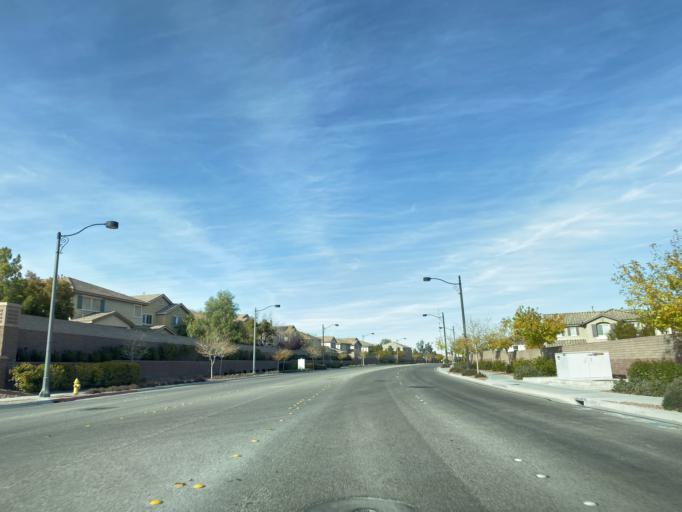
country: US
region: Nevada
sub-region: Clark County
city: Summerlin South
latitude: 36.3040
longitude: -115.3215
